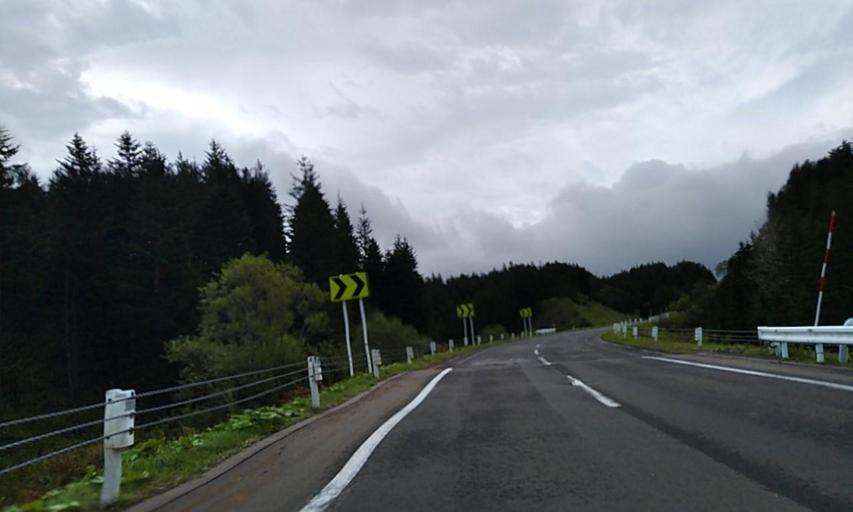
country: JP
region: Hokkaido
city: Abashiri
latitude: 43.6234
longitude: 144.5801
